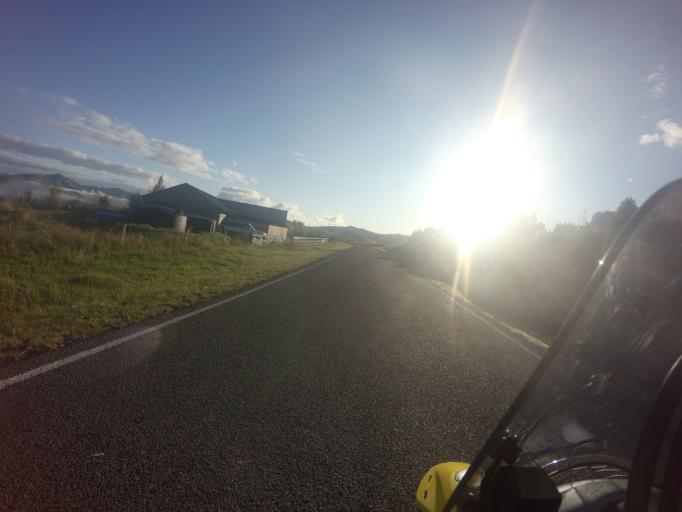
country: NZ
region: Gisborne
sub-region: Gisborne District
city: Gisborne
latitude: -38.6619
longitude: 178.0680
